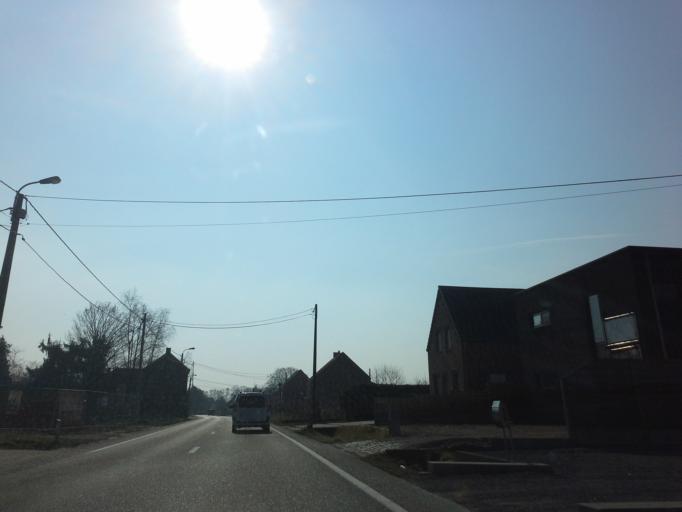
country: BE
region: Flanders
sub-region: Provincie Antwerpen
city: Meerhout
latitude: 51.1191
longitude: 5.0922
